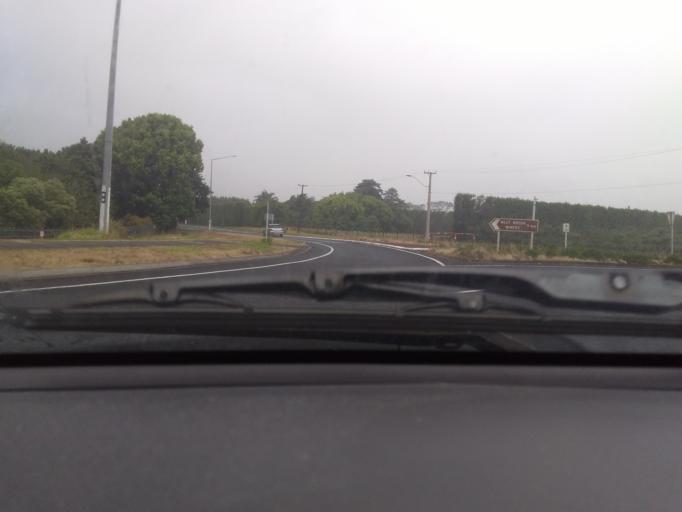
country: NZ
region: Auckland
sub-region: Auckland
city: Rosebank
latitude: -36.7872
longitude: 174.5768
